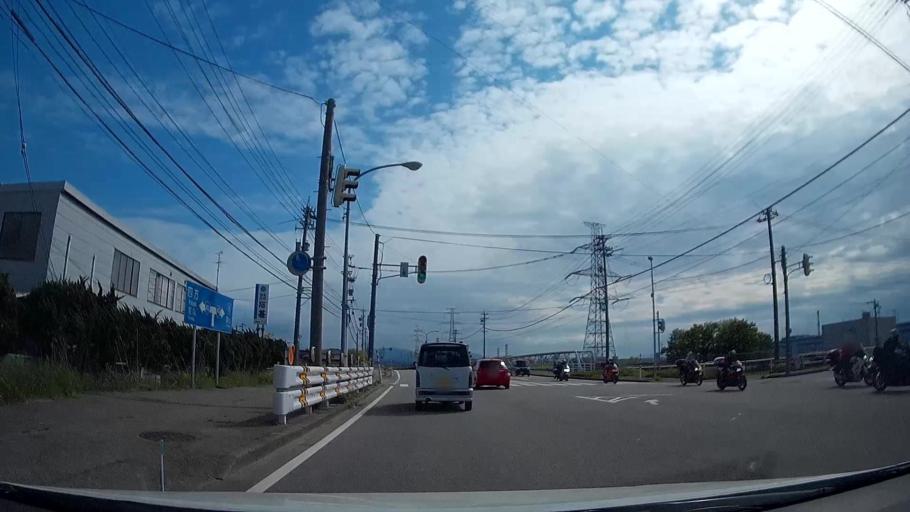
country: JP
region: Toyama
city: Kuragaki-kosugi
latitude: 36.7545
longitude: 137.1323
